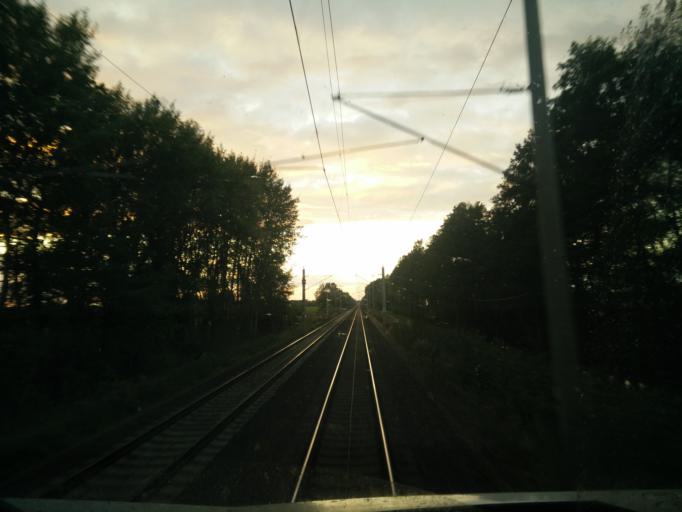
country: DE
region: Brandenburg
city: Wusterhausen
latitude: 52.8688
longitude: 12.4214
